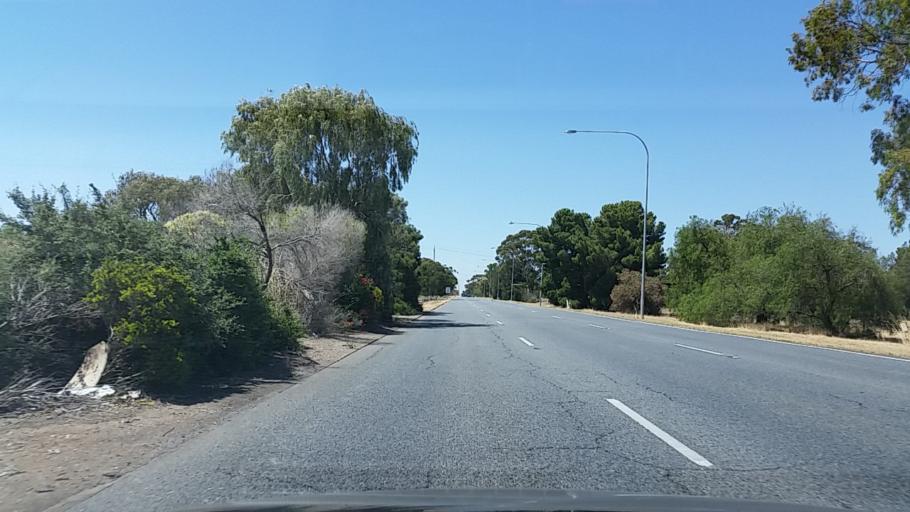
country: AU
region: South Australia
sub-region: Playford
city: Smithfield
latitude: -34.6977
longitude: 138.6843
